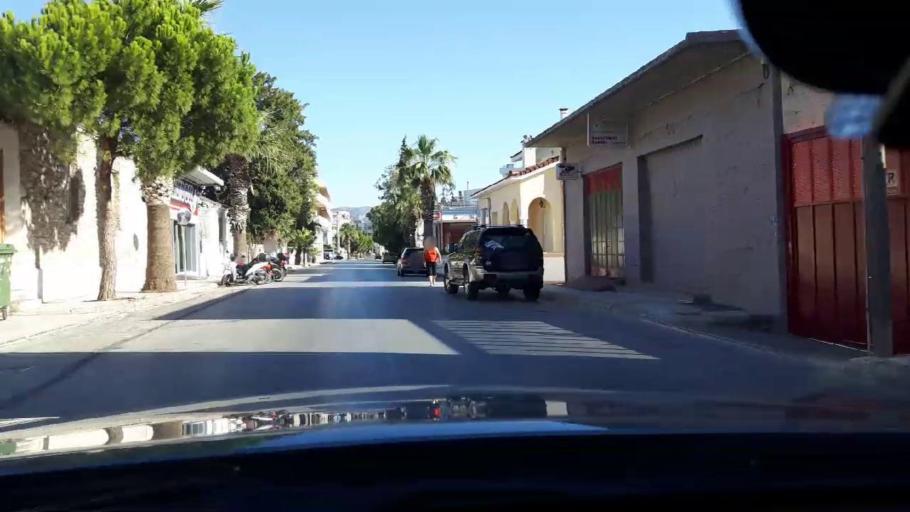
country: GR
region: Attica
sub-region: Nomarchia Anatolikis Attikis
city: Markopoulo
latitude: 37.8797
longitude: 23.9333
